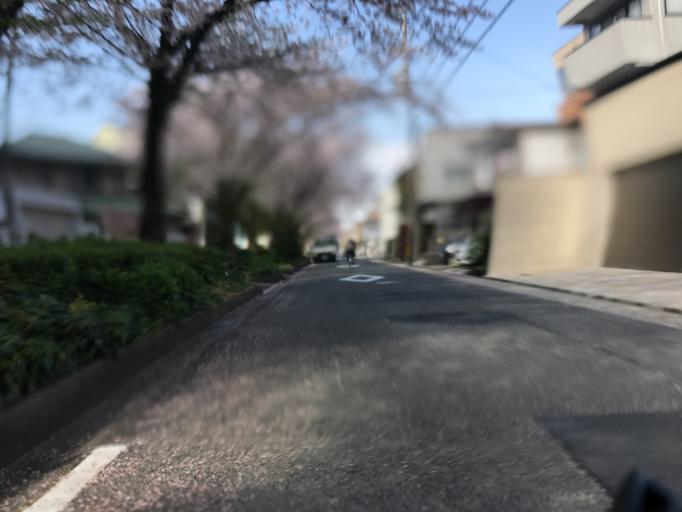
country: JP
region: Aichi
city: Nagoya-shi
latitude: 35.1725
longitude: 136.9460
